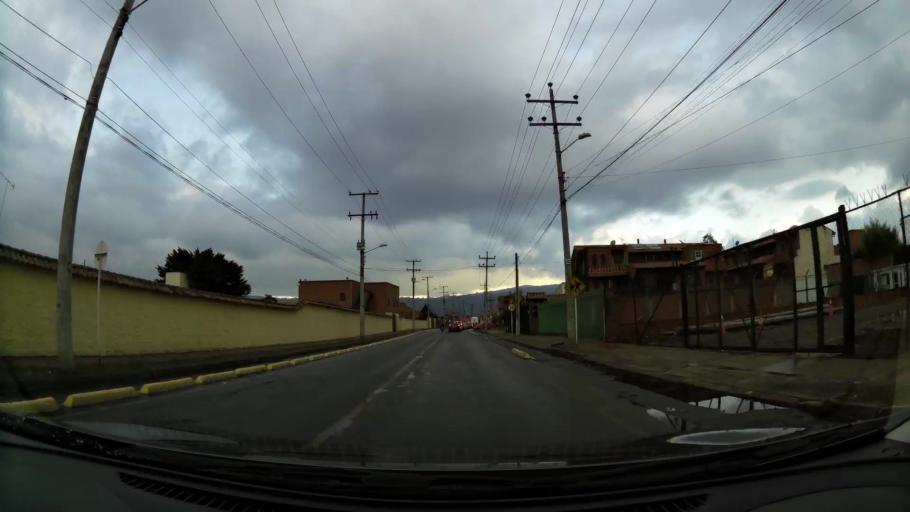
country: CO
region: Cundinamarca
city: Chia
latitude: 4.8693
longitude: -74.0566
